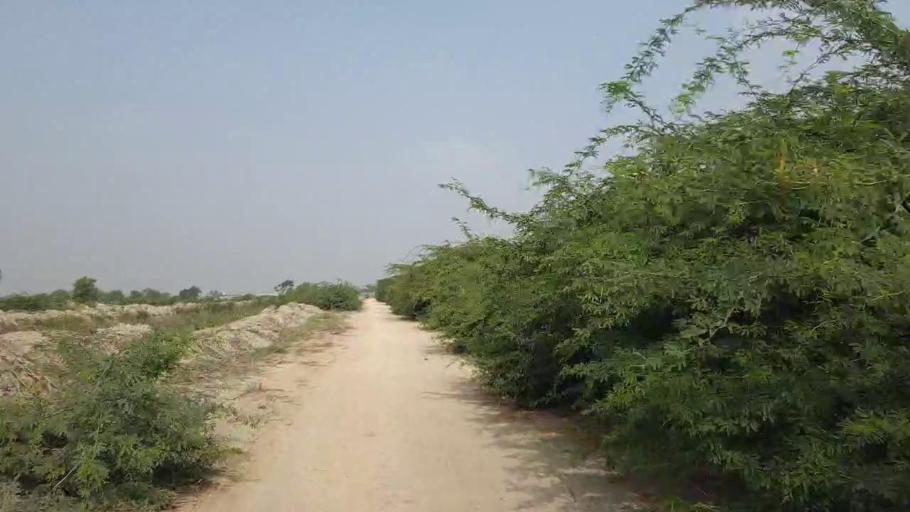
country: PK
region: Sindh
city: Kario
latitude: 24.7778
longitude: 68.5219
